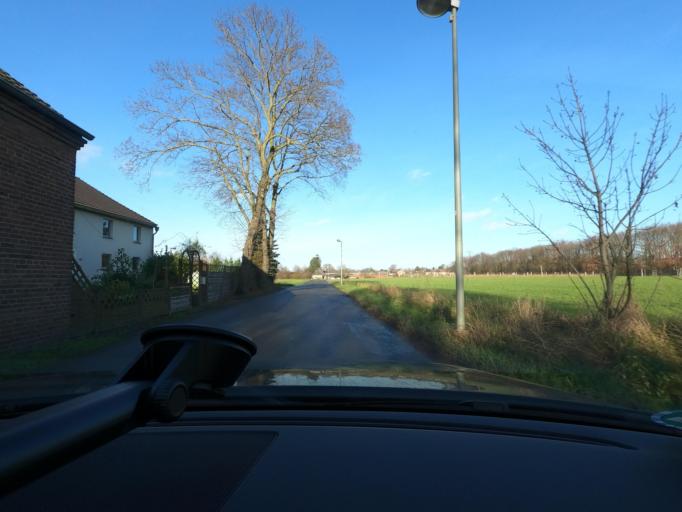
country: DE
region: North Rhine-Westphalia
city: Tonisvorst
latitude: 51.3428
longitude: 6.5203
